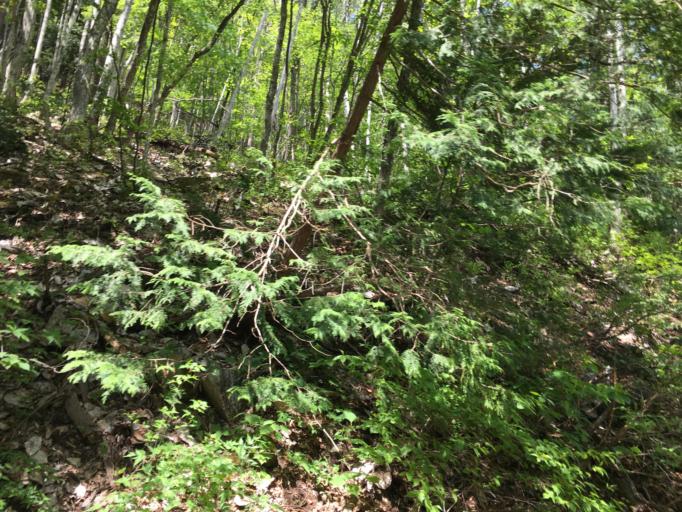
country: JP
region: Nagano
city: Omachi
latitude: 36.5112
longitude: 137.7952
